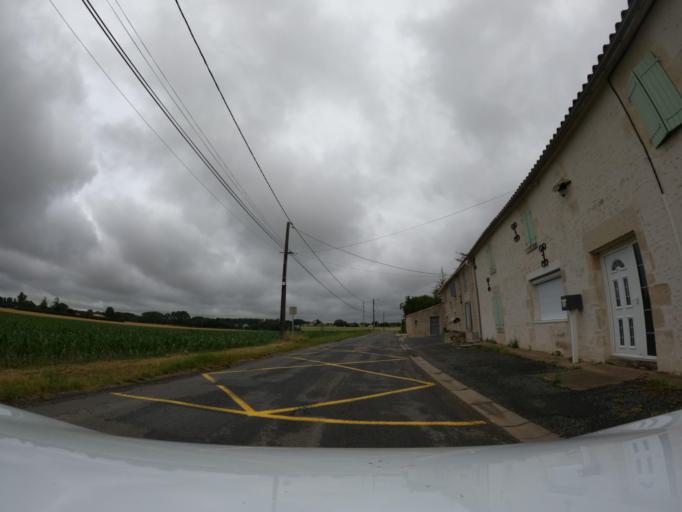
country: FR
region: Pays de la Loire
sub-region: Departement de la Vendee
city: Maillezais
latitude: 46.4050
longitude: -0.7359
